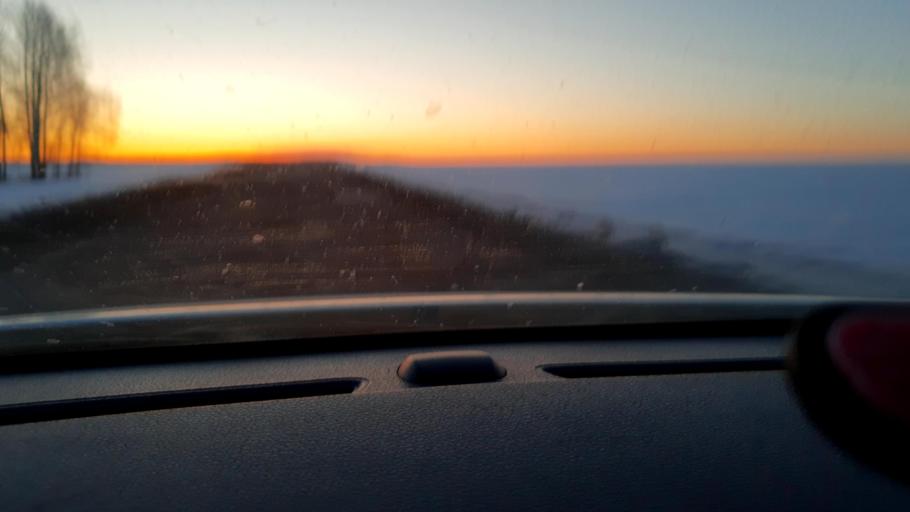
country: RU
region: Bashkortostan
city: Avdon
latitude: 54.3879
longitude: 55.7680
